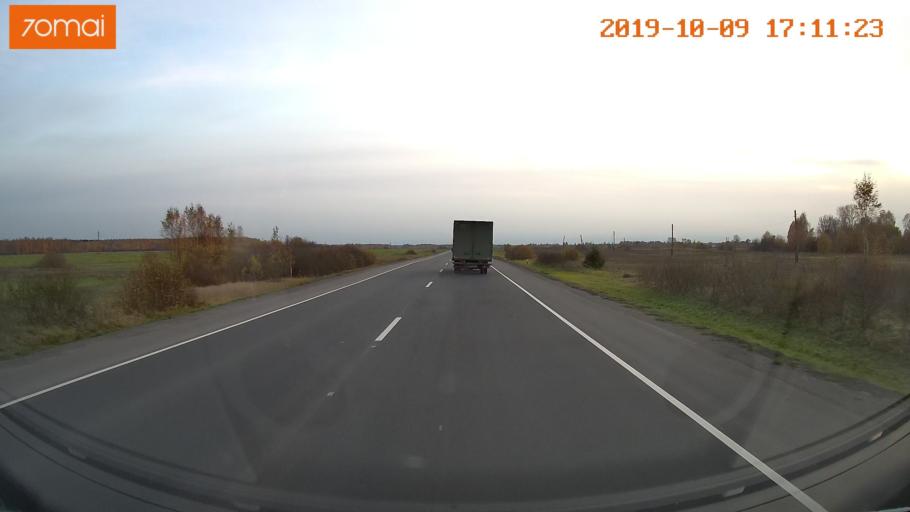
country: RU
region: Ivanovo
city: Privolzhsk
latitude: 57.3435
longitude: 41.2506
